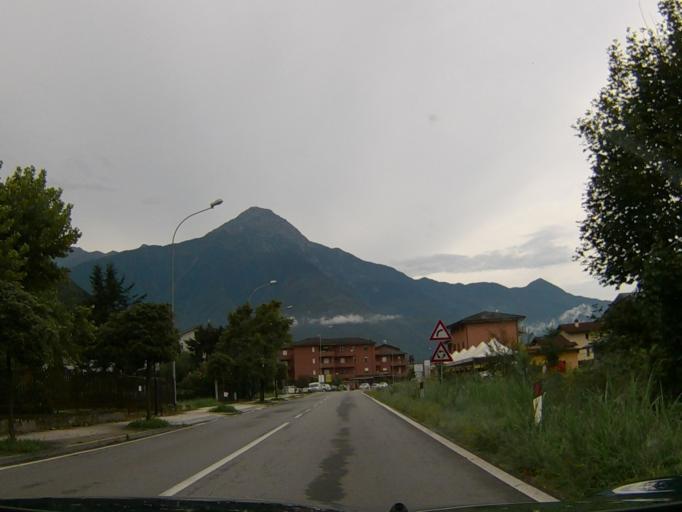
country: IT
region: Lombardy
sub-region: Provincia di Sondrio
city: Dubino
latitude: 46.1730
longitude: 9.4337
